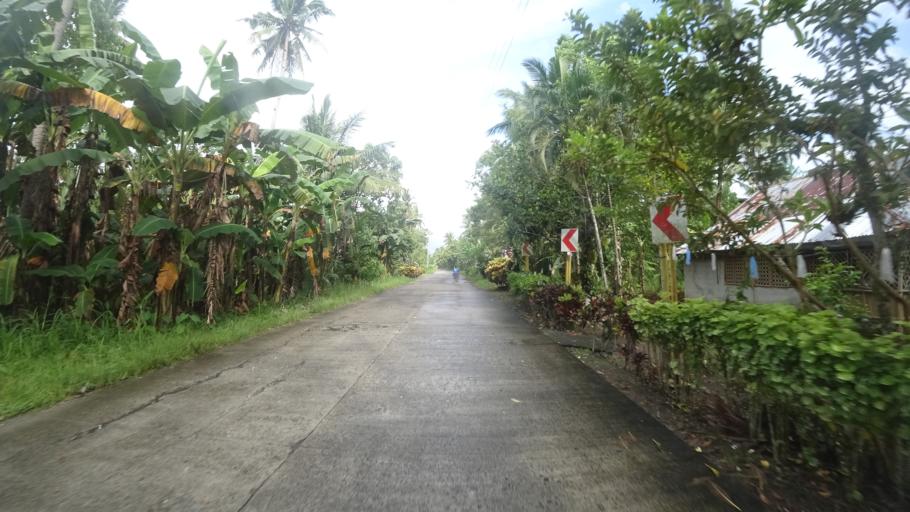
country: PH
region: Eastern Visayas
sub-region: Province of Leyte
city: MacArthur
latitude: 10.8181
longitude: 124.9655
